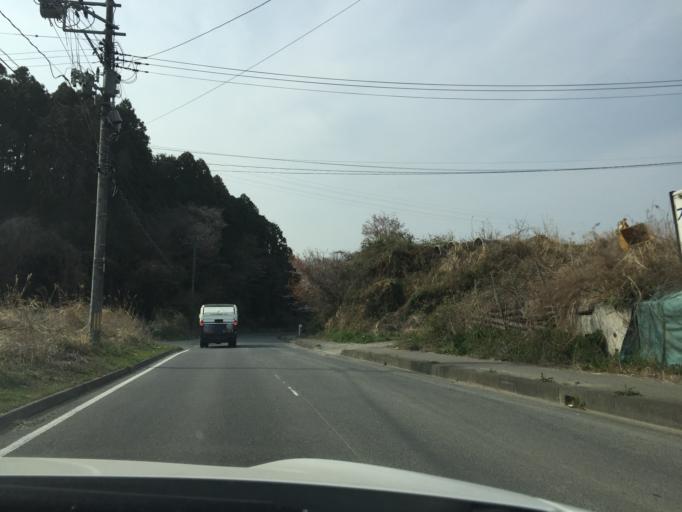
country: JP
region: Fukushima
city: Iwaki
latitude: 36.9654
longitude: 140.8498
